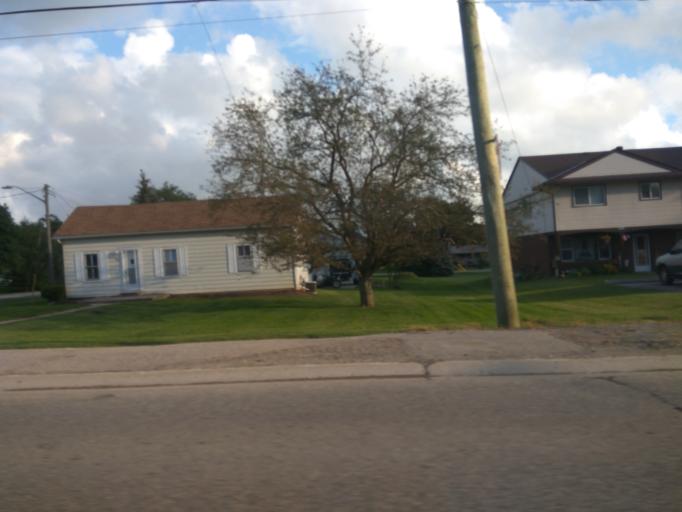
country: CA
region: Ontario
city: Stratford
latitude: 43.3696
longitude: -80.8335
